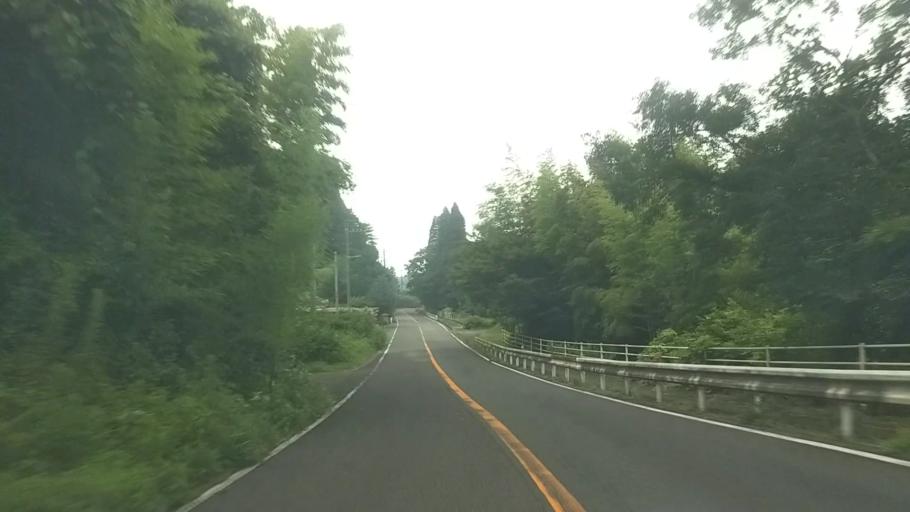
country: JP
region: Chiba
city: Katsuura
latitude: 35.2445
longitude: 140.1919
